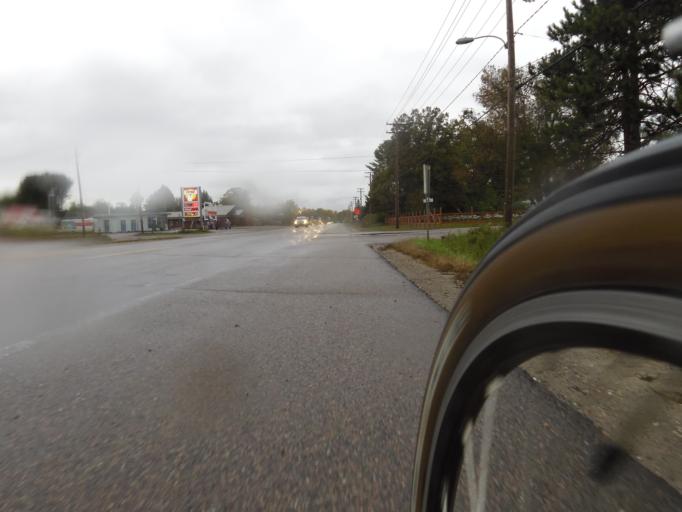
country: CA
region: Quebec
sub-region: Outaouais
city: Fort-Coulonge
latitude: 45.8522
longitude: -76.7323
